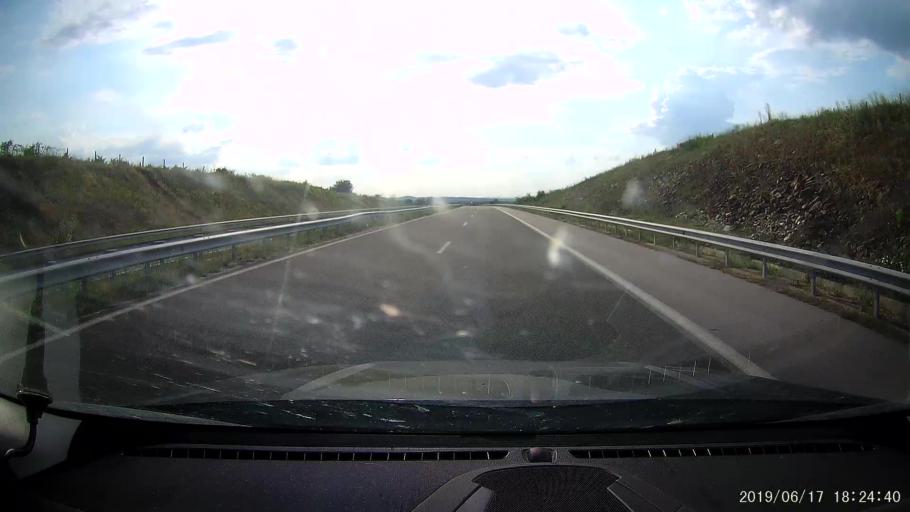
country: BG
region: Khaskovo
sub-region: Obshtina Dimitrovgrad
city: Dimitrovgrad
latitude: 41.9866
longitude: 25.6851
